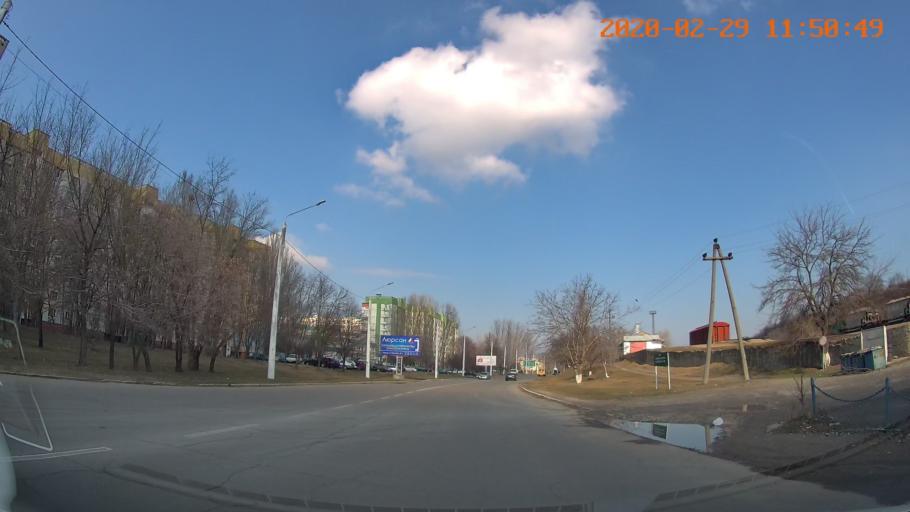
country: MD
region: Telenesti
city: Ribnita
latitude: 47.7612
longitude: 28.9897
